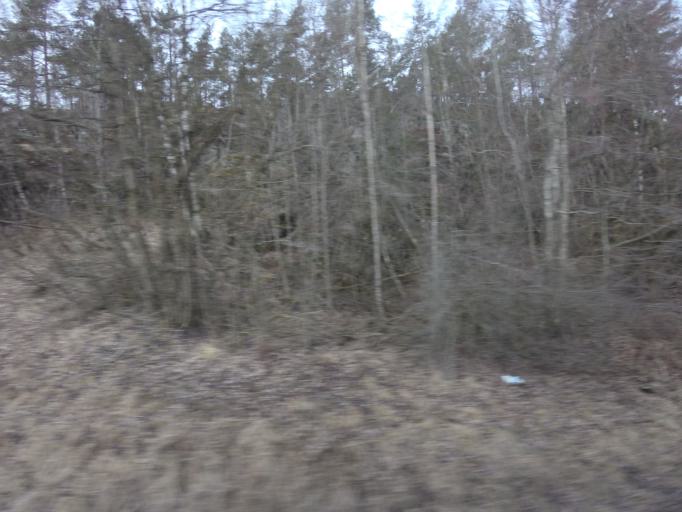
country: NO
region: Akershus
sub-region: Enebakk
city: Flateby
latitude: 59.8357
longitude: 11.2450
